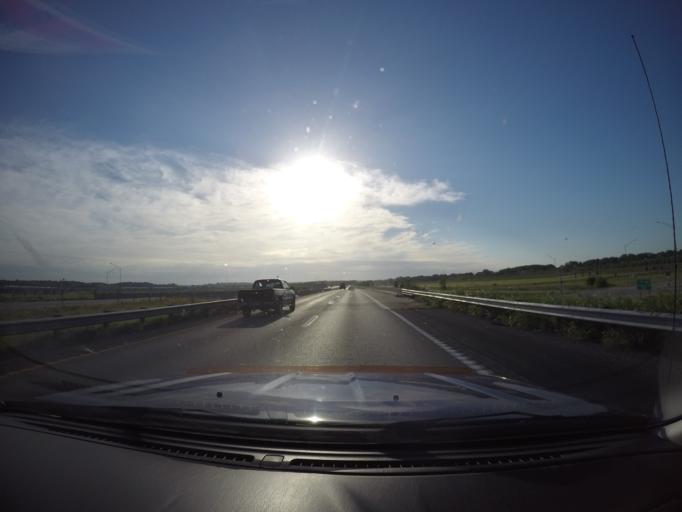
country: US
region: Missouri
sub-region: Platte County
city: Riverside
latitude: 39.1602
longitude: -94.6418
